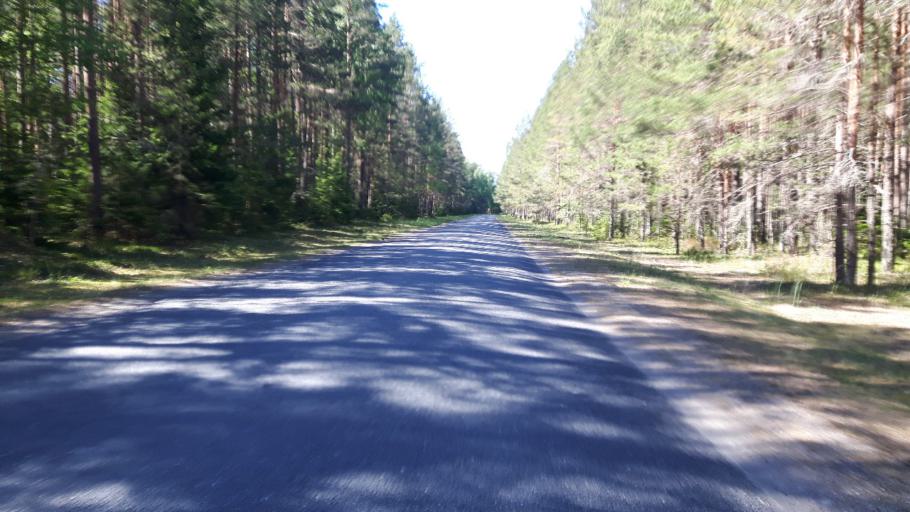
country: EE
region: Harju
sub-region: Loksa linn
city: Loksa
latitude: 59.5654
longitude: 25.6941
